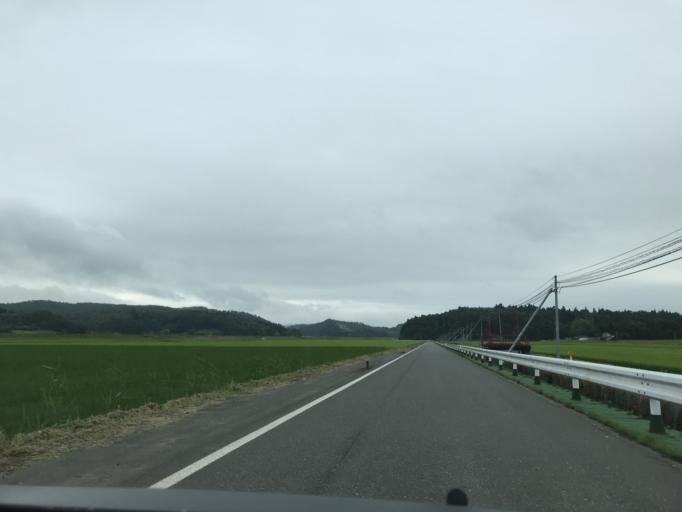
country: JP
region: Iwate
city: Ichinoseki
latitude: 38.8150
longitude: 141.2023
